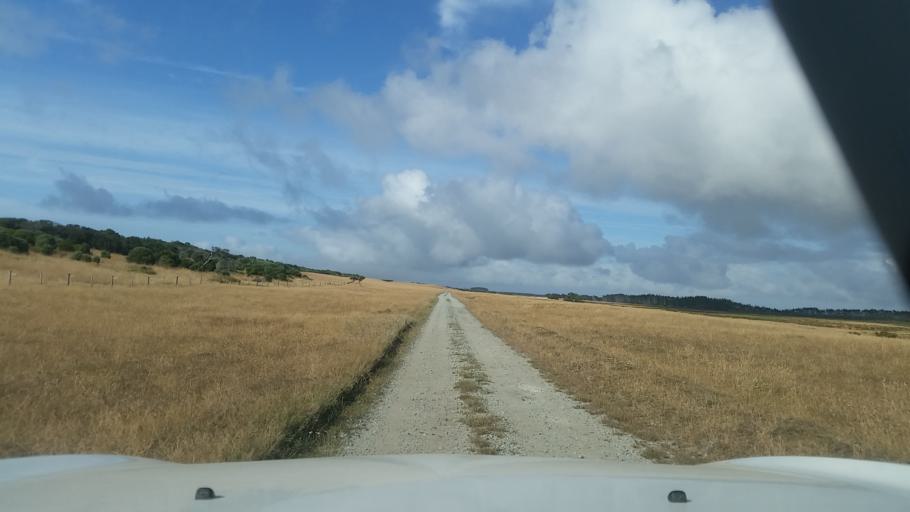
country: NZ
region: Chatham Islands
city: Waitangi
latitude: -43.7870
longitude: -176.3372
